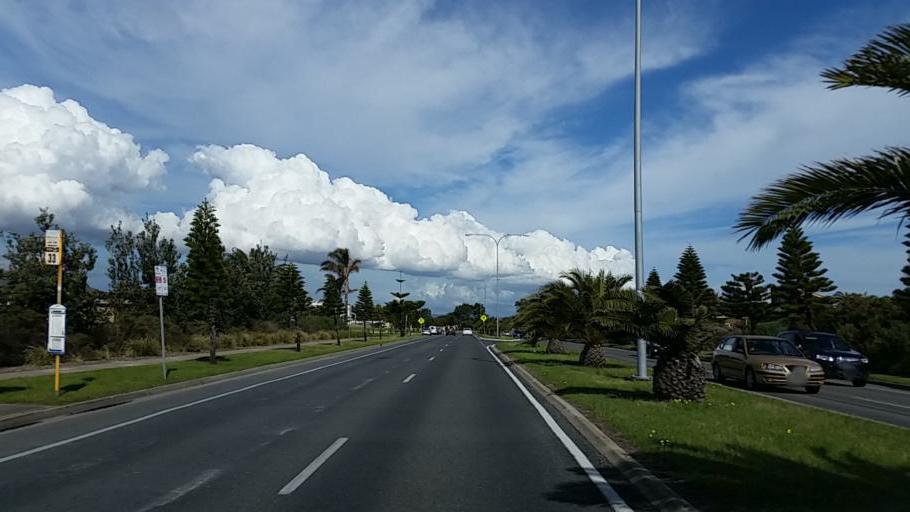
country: AU
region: South Australia
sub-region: Charles Sturt
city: West Lakes Shore
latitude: -34.8737
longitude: 138.4833
